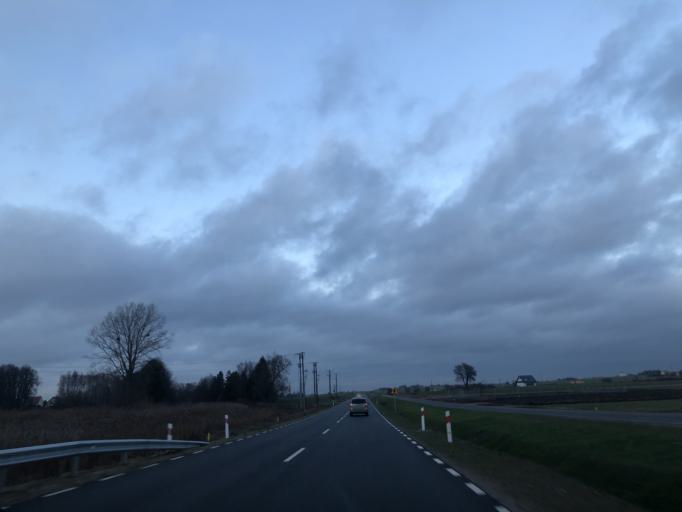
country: PL
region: Podlasie
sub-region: Lomza
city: Lomza
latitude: 53.1343
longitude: 22.0497
